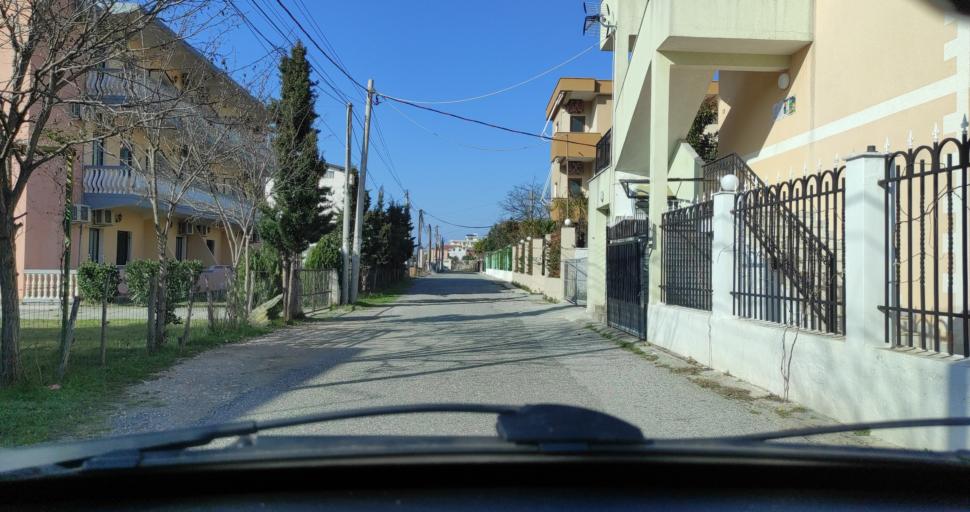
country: AL
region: Shkoder
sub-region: Rrethi i Shkodres
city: Velipoje
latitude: 41.8640
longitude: 19.4300
